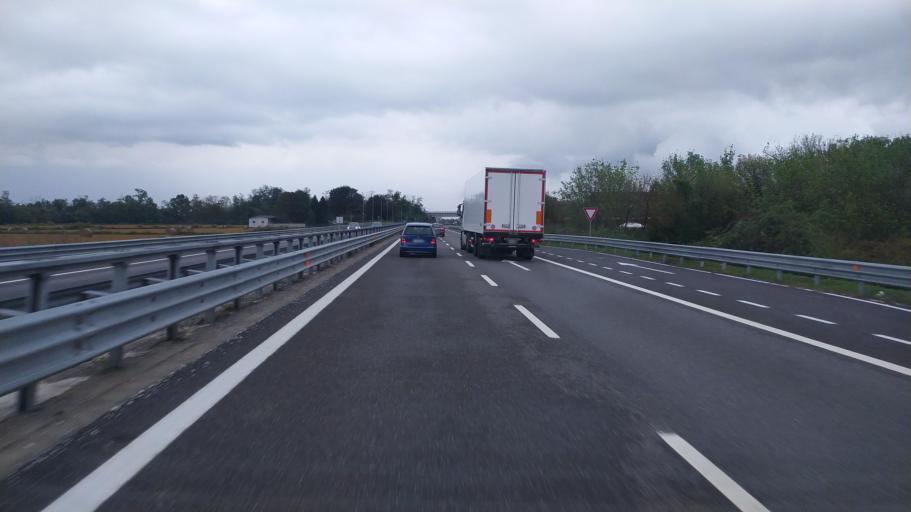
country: IT
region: Lombardy
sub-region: Provincia di Pavia
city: Torre d'Isola
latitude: 45.2110
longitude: 9.1041
